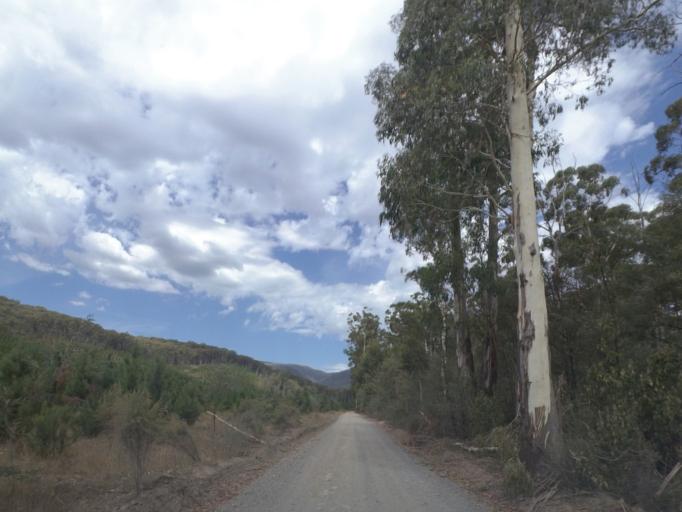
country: AU
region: Victoria
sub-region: Murrindindi
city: Alexandra
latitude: -37.3723
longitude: 145.7576
